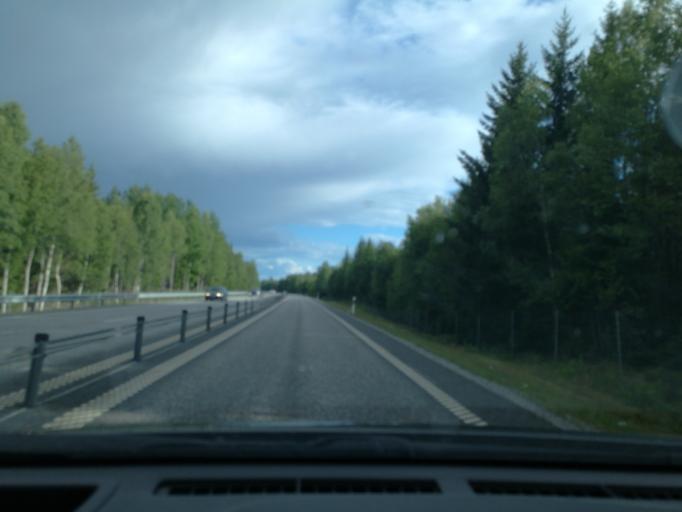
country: SE
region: Vaestmanland
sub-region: Surahammars Kommun
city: Surahammar
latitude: 59.7340
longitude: 16.2292
